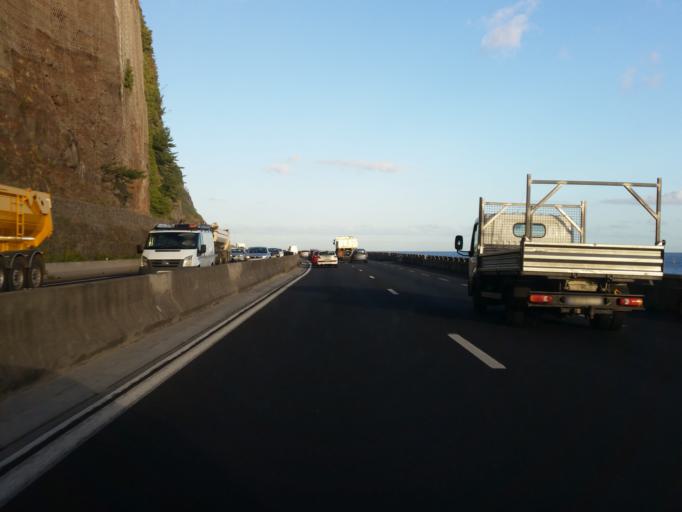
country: RE
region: Reunion
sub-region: Reunion
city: Saint-Denis
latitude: -20.8787
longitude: 55.4087
